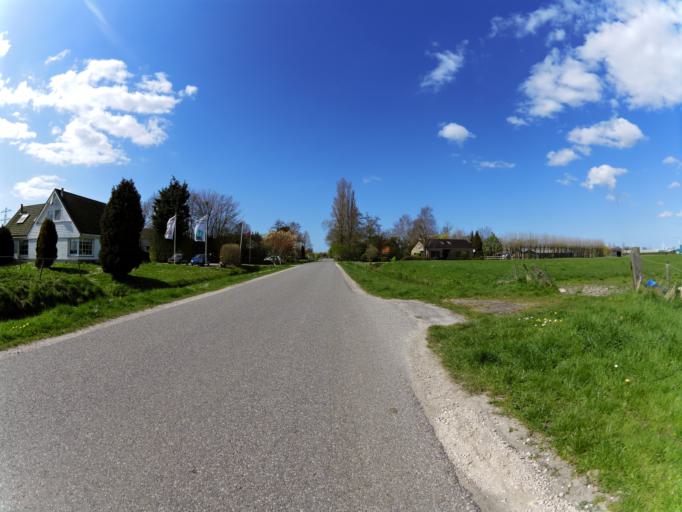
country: NL
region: South Holland
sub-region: Gemeente Brielle
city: Brielle
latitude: 51.9014
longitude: 4.1465
